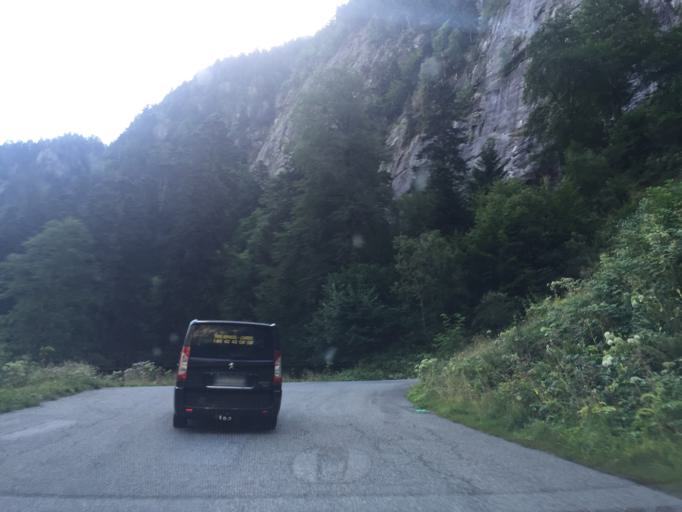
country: FR
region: Midi-Pyrenees
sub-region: Departement des Hautes-Pyrenees
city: Cauterets
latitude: 42.8614
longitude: -0.1204
